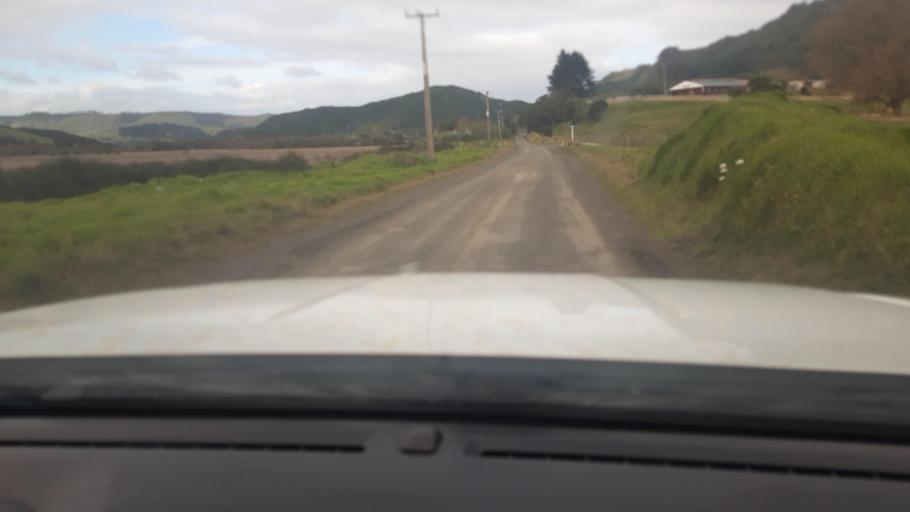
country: NZ
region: Northland
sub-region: Far North District
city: Ahipara
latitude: -35.2576
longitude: 173.2033
